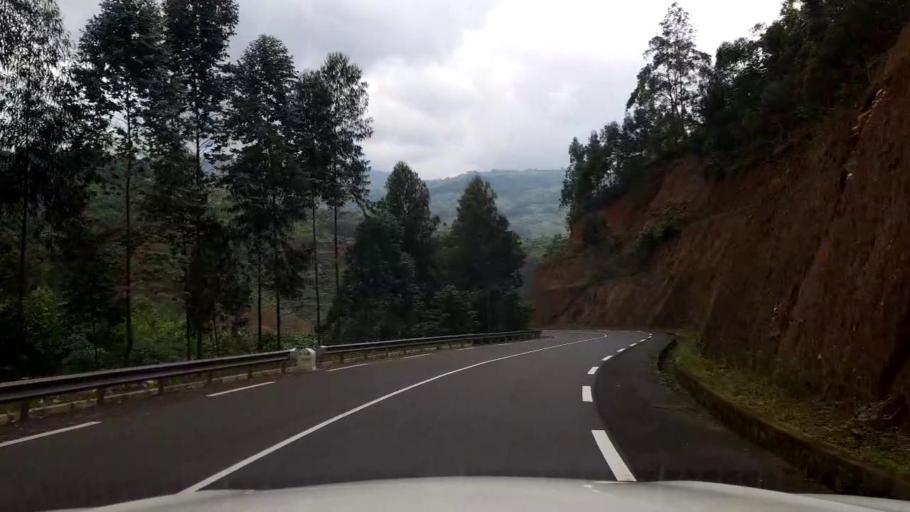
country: RW
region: Western Province
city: Kibuye
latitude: -1.9091
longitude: 29.3660
